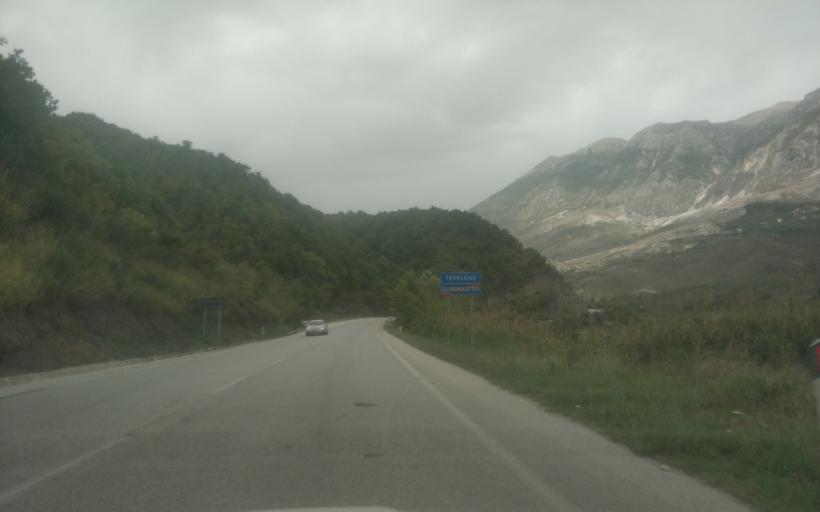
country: AL
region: Gjirokaster
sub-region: Rrethi i Gjirokastres
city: Picar
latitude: 40.2166
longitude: 20.0861
